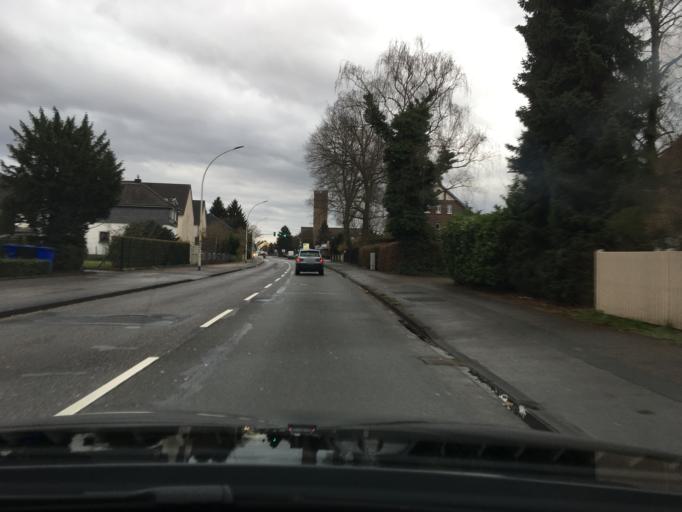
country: DE
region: North Rhine-Westphalia
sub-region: Regierungsbezirk Dusseldorf
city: Hilden
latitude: 51.1850
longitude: 6.9248
